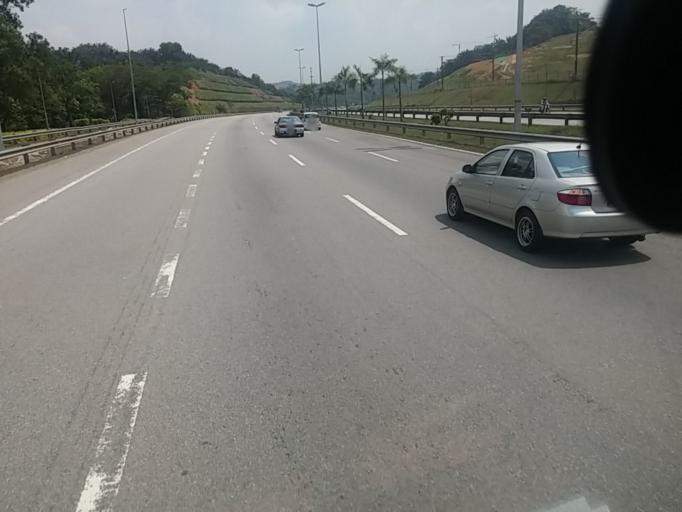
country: MY
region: Putrajaya
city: Putrajaya
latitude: 2.9474
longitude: 101.6609
